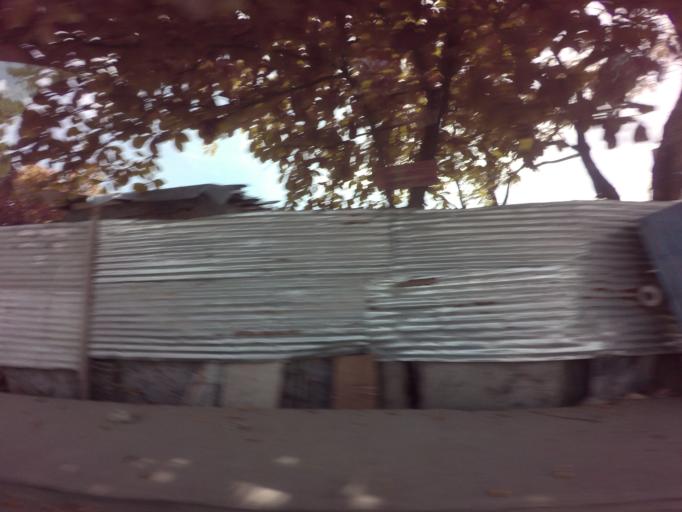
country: PH
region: Calabarzon
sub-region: Province of Rizal
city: Taguig
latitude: 14.5270
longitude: 121.0890
